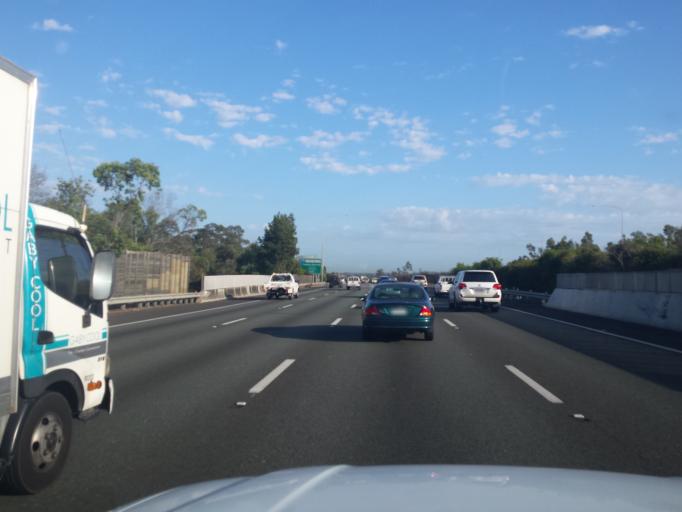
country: AU
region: Queensland
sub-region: Gold Coast
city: Yatala
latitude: -27.7399
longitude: 153.2310
